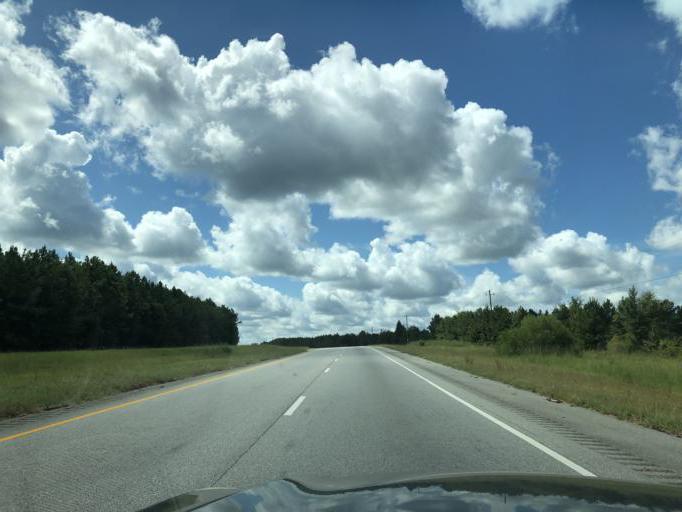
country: US
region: Alabama
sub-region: Russell County
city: Ladonia
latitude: 32.2258
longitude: -85.1709
